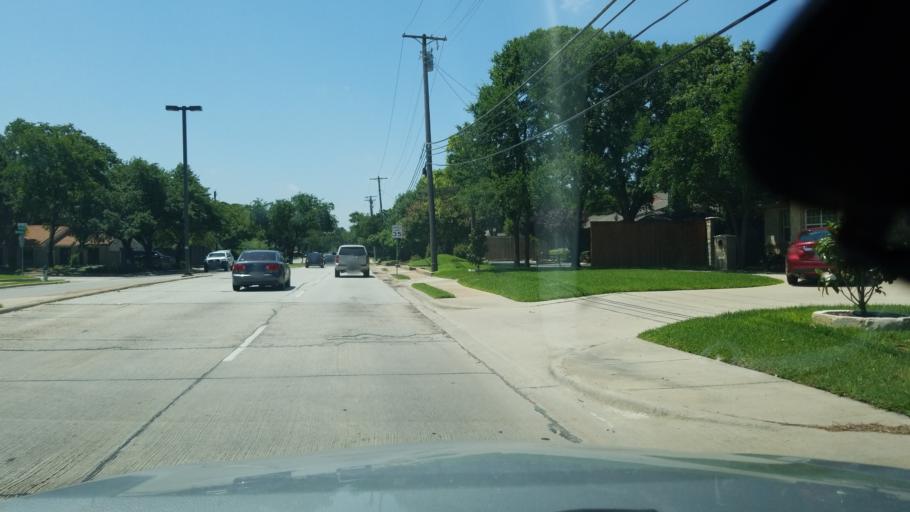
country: US
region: Texas
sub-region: Dallas County
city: Irving
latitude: 32.8275
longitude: -96.9592
